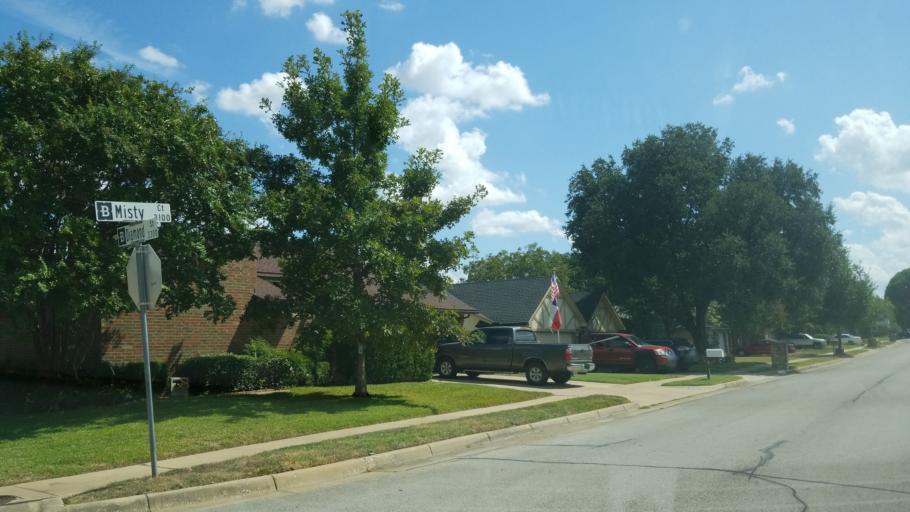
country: US
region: Texas
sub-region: Tarrant County
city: Bedford
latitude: 32.8573
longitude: -97.1125
